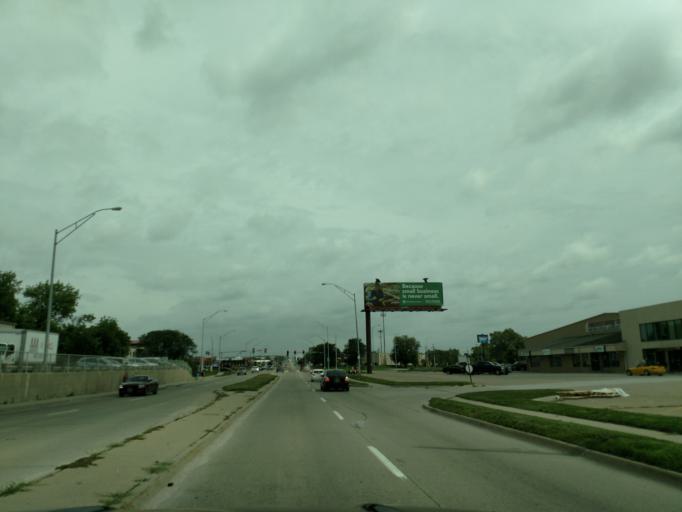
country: US
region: Nebraska
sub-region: Sarpy County
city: La Vista
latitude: 41.2004
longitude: -96.0238
